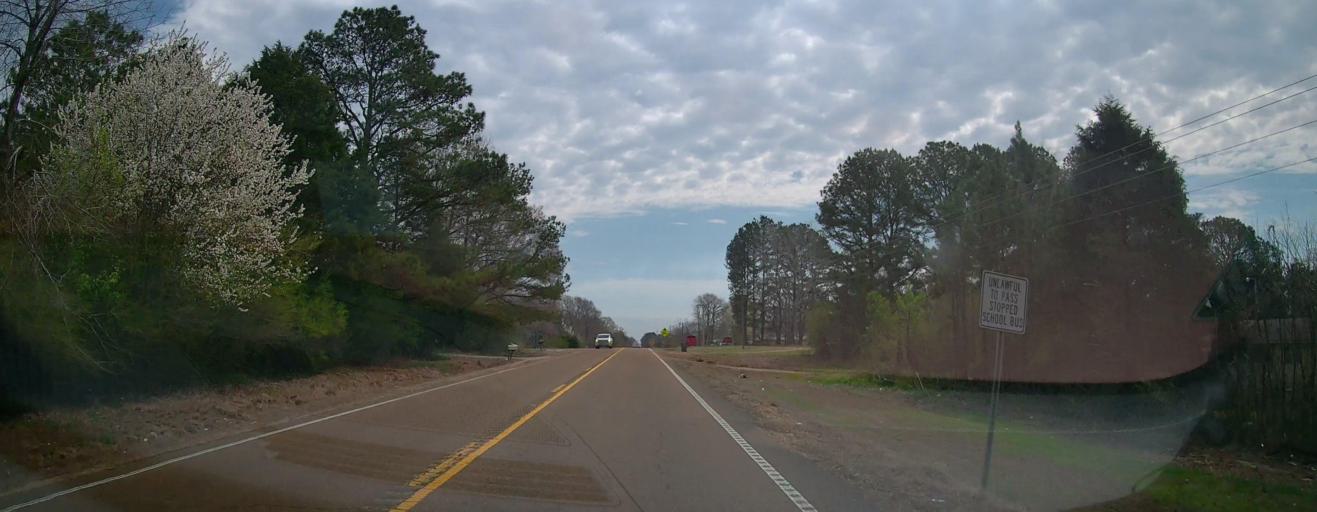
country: US
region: Mississippi
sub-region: Marshall County
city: Holly Springs
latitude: 34.8239
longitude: -89.5522
